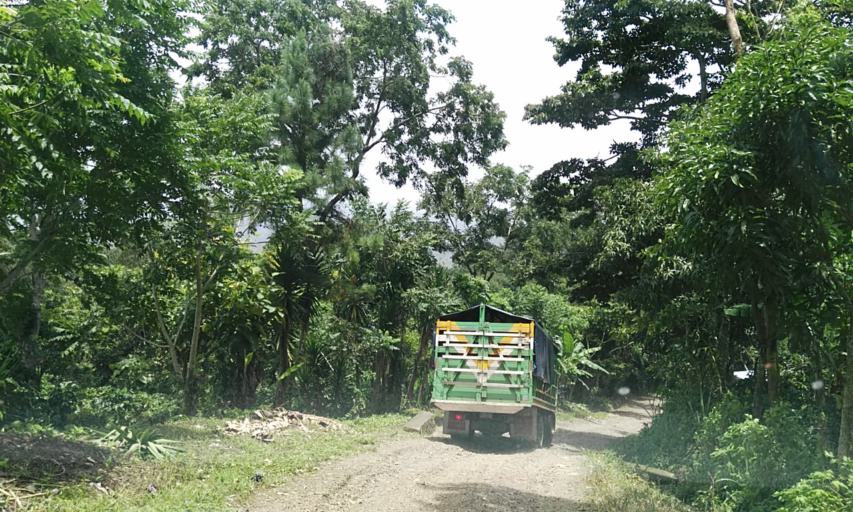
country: NI
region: Matagalpa
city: Matagalpa
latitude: 13.0119
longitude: -85.8769
